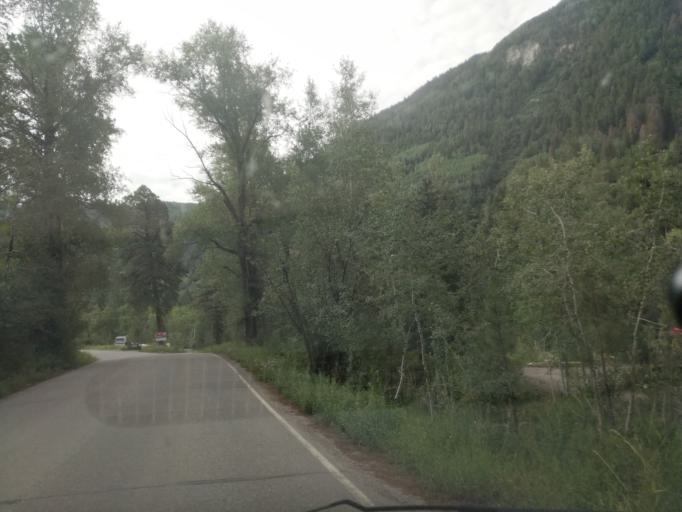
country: US
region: Colorado
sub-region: Gunnison County
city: Crested Butte
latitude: 39.0710
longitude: -107.1979
